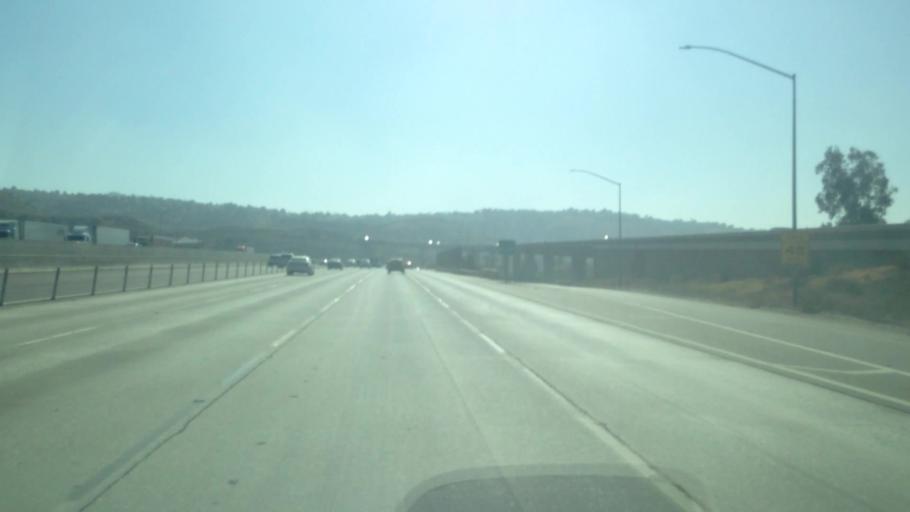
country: US
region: California
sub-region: Orange County
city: Yorba Linda
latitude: 33.8700
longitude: -117.7120
